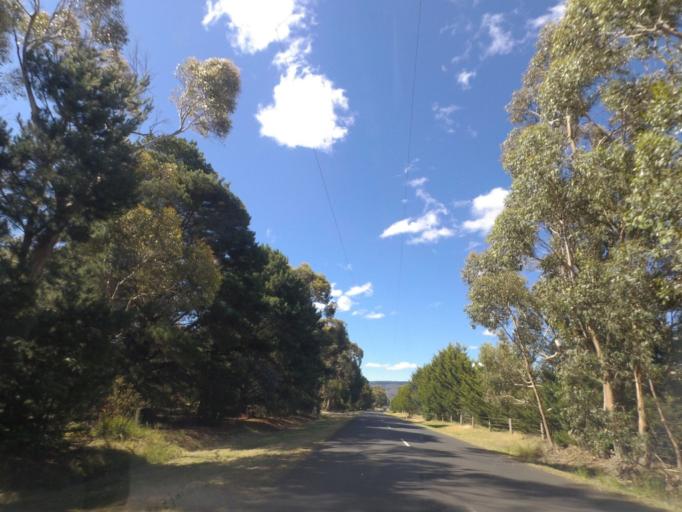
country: AU
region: Victoria
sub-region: Hume
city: Sunbury
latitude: -37.4497
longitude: 144.6017
